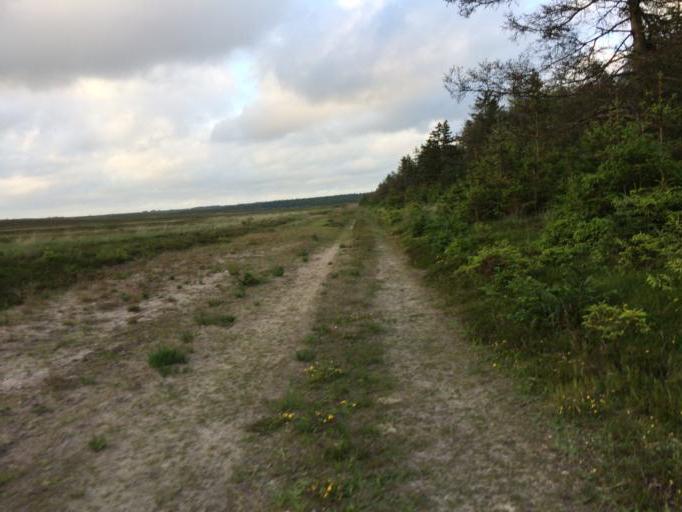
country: DK
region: Central Jutland
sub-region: Holstebro Kommune
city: Ulfborg
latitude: 56.2764
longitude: 8.4497
